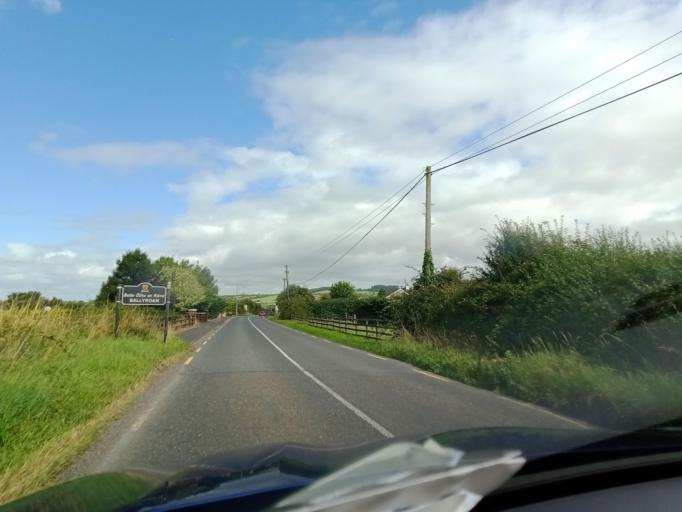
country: IE
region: Leinster
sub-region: Laois
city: Abbeyleix
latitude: 52.9438
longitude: -7.3160
